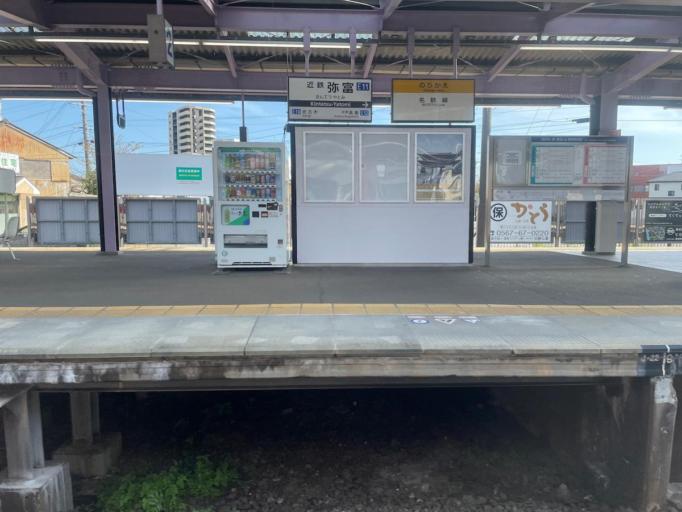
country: JP
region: Aichi
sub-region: Aisai-shi
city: Aisai
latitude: 35.1137
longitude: 136.7281
